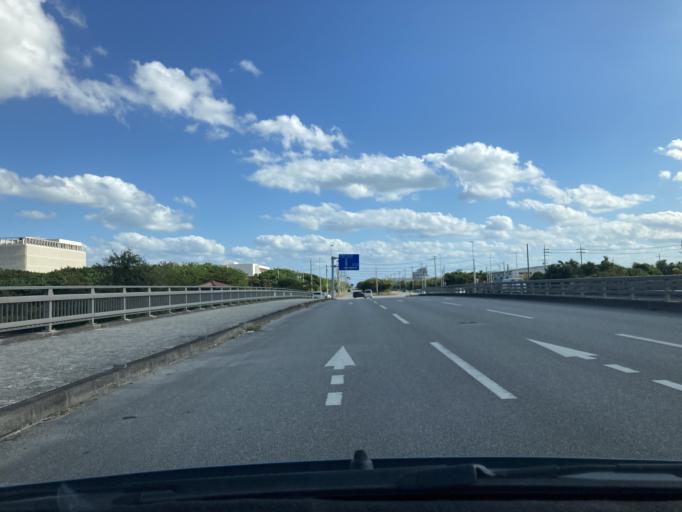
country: JP
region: Okinawa
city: Gushikawa
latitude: 26.3427
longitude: 127.8568
